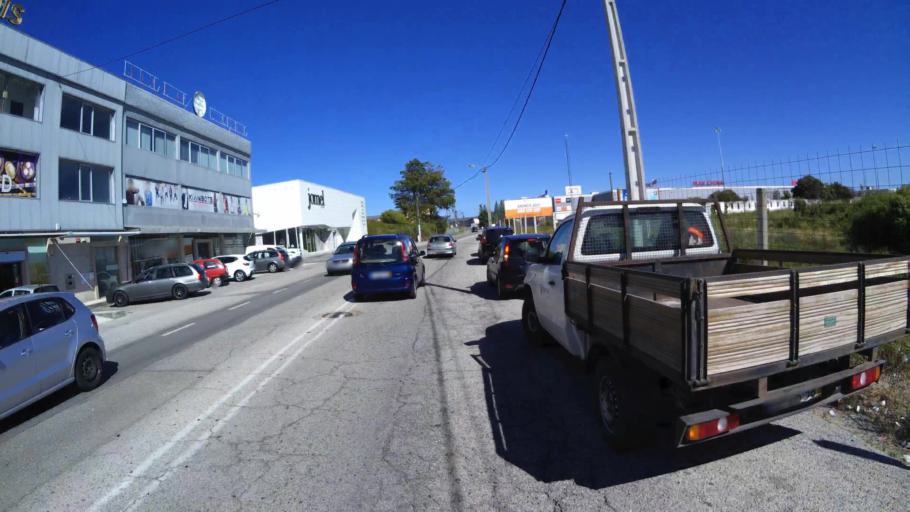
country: PT
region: Aveiro
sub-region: Aveiro
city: Aveiro
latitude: 40.6528
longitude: -8.6151
